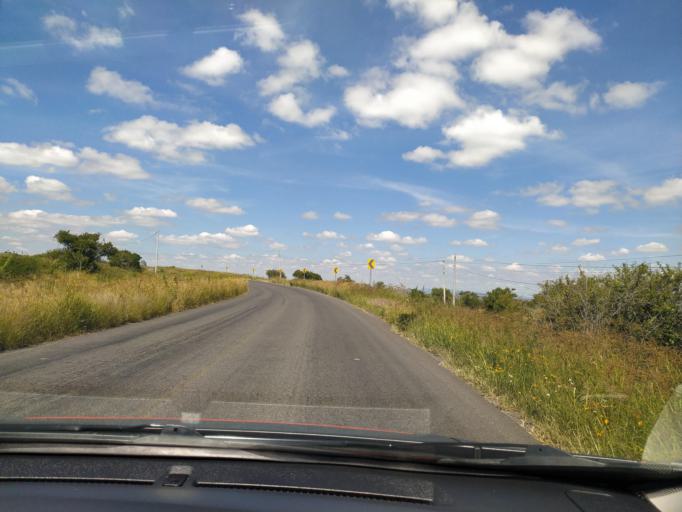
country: MX
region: Jalisco
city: San Diego de Alejandria
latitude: 21.0070
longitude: -102.0109
